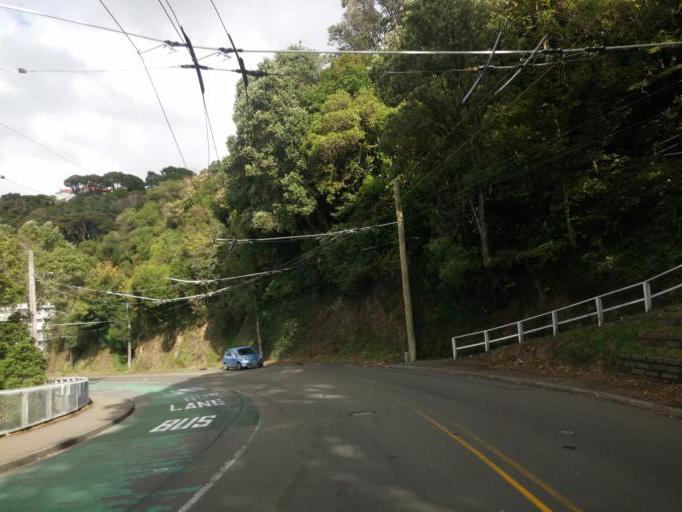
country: NZ
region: Wellington
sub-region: Wellington City
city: Kelburn
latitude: -41.2826
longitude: 174.7524
